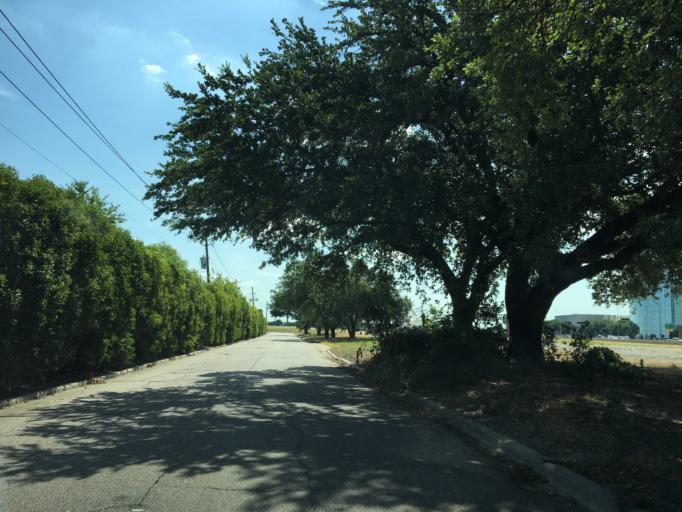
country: US
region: Texas
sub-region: Dallas County
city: Farmers Branch
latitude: 32.9132
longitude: -96.8799
